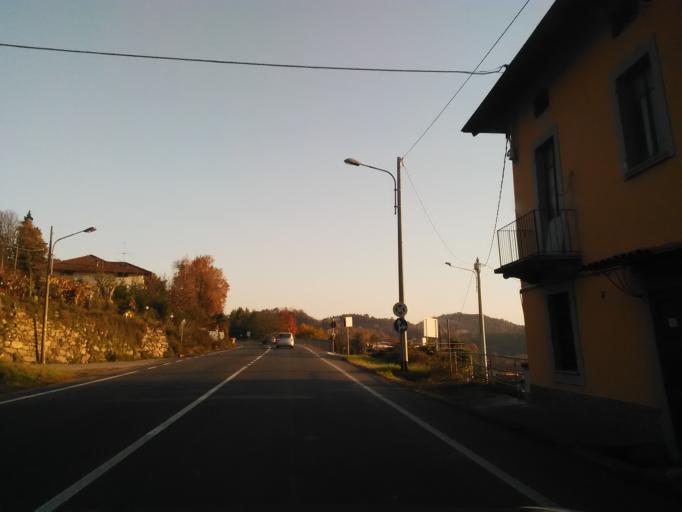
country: IT
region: Piedmont
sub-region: Provincia di Biella
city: Roppolo
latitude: 45.4166
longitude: 8.0660
